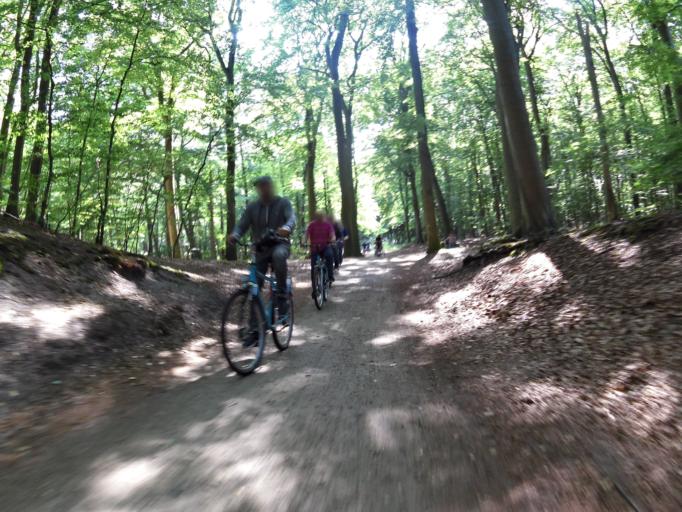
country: DE
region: Mecklenburg-Vorpommern
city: Ostseebad Zinnowitz
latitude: 54.0758
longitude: 13.9264
